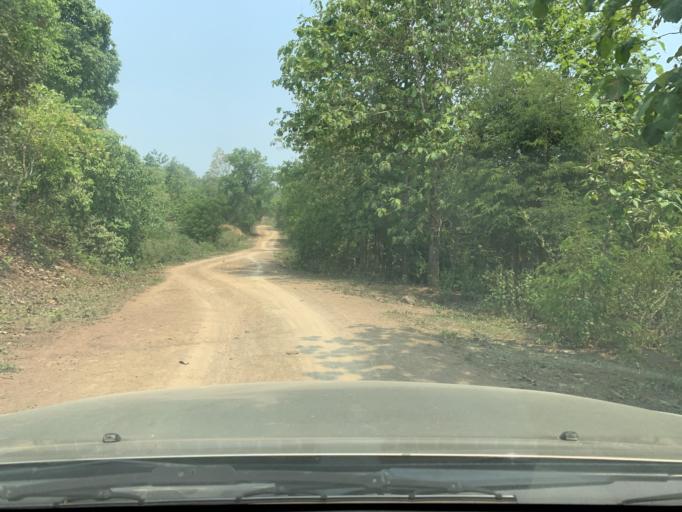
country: LA
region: Louangphabang
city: Louangphabang
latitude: 19.9413
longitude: 102.1333
